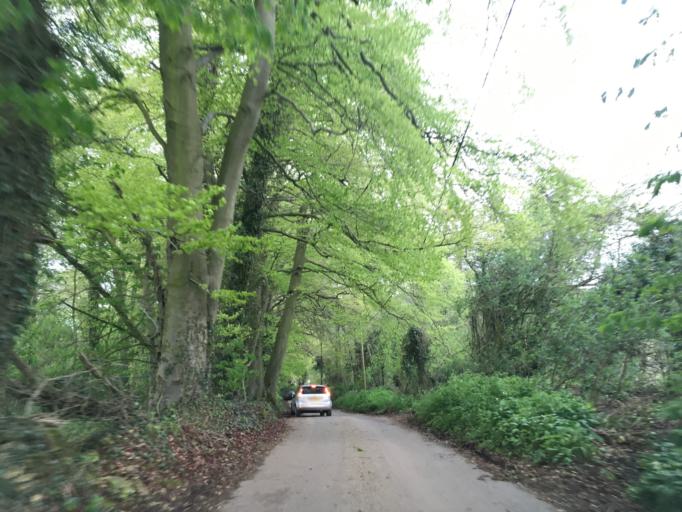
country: GB
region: England
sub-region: Gloucestershire
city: Wotton-under-Edge
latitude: 51.6400
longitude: -2.3319
